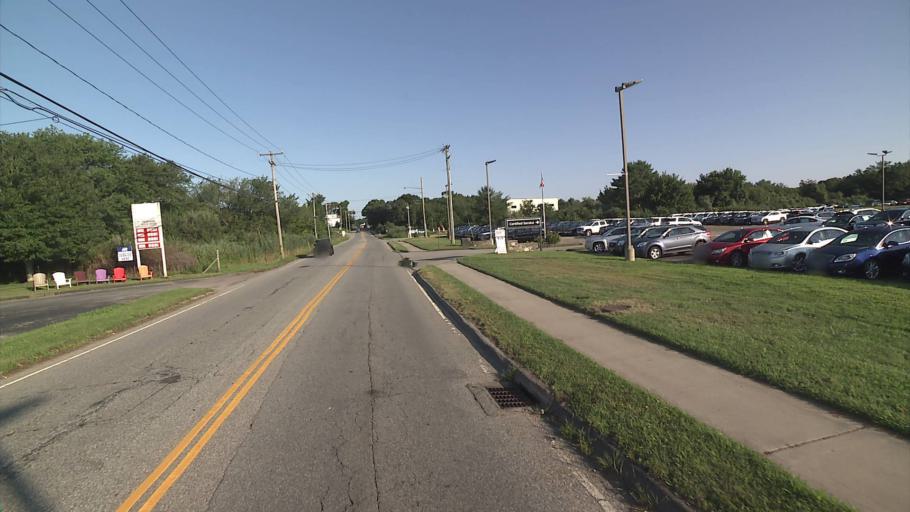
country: US
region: Connecticut
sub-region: New London County
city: Mystic
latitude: 41.3455
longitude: -71.9524
